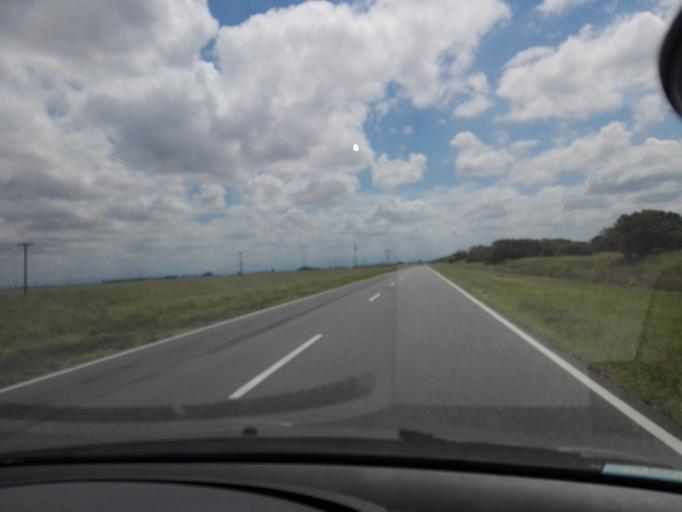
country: AR
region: Cordoba
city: Toledo
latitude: -31.6457
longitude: -64.0284
